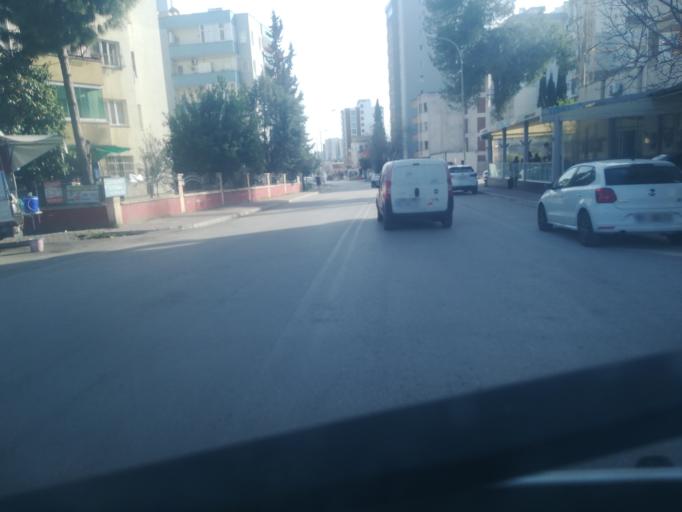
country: TR
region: Adana
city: Adana
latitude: 37.0384
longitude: 35.3127
